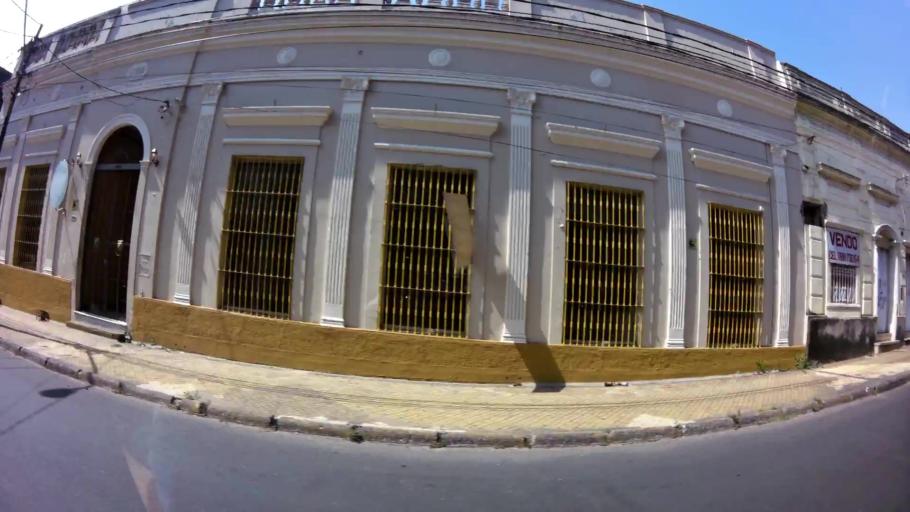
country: PY
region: Asuncion
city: Asuncion
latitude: -25.2867
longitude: -57.6269
